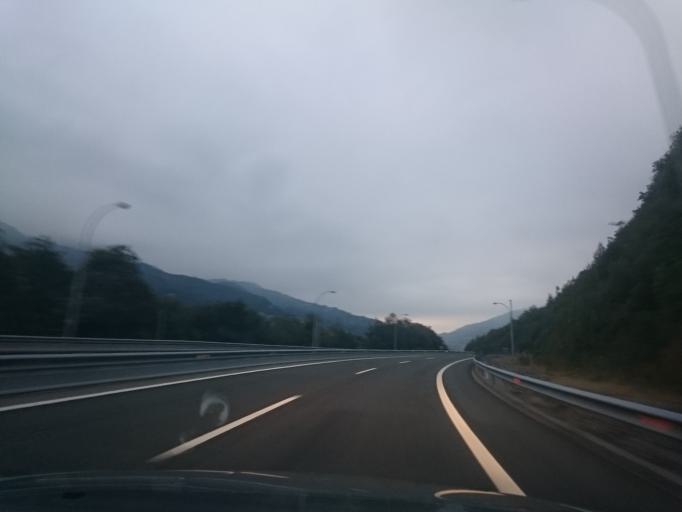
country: ES
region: Asturias
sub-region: Province of Asturias
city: Pola de Lena
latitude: 43.0906
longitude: -5.8232
